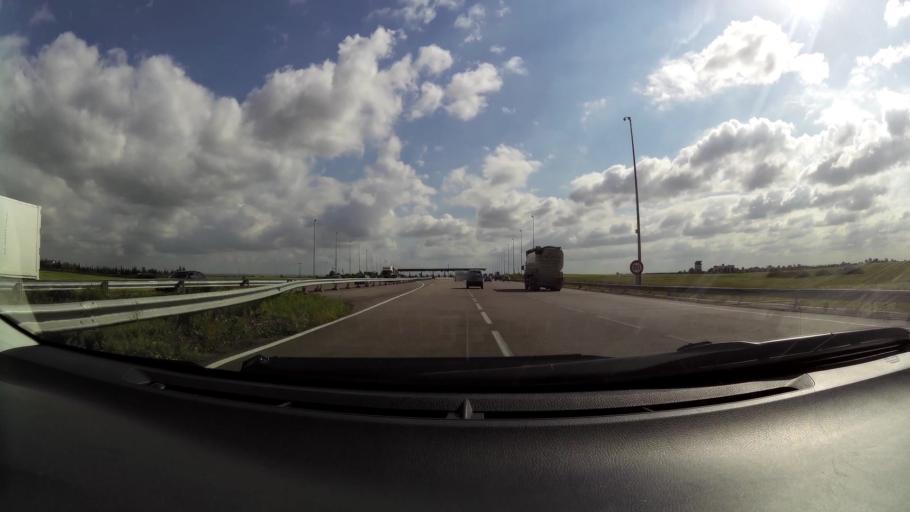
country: MA
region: Chaouia-Ouardigha
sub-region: Settat Province
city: Berrechid
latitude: 33.2353
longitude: -7.5712
